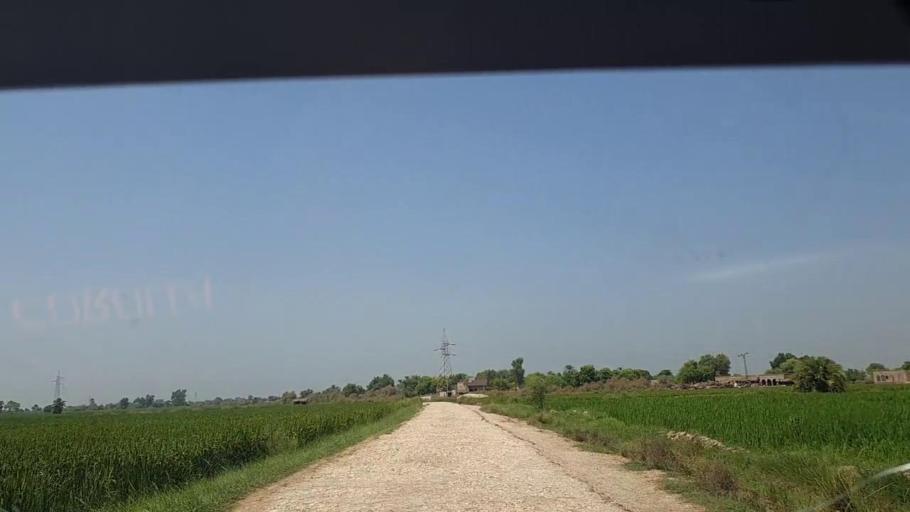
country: PK
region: Sindh
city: Ghauspur
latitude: 28.1866
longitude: 69.0913
